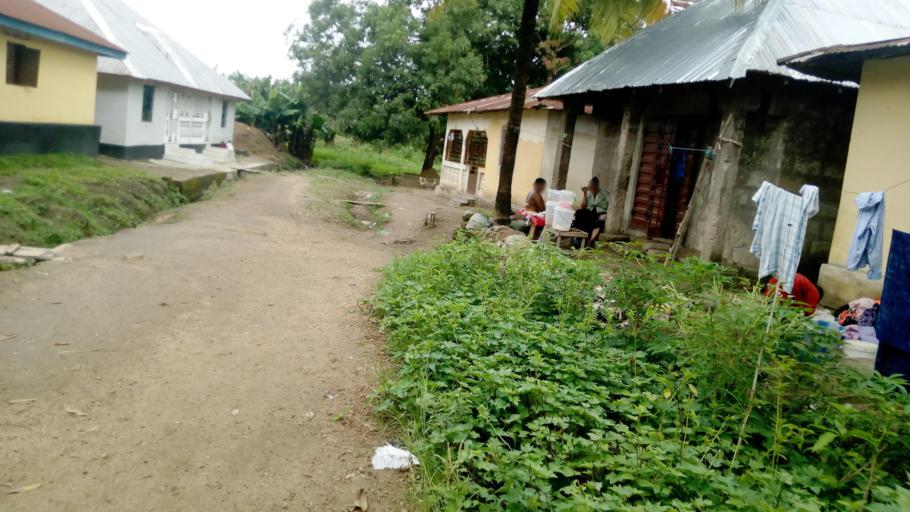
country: SL
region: Northern Province
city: Makeni
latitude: 8.8940
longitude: -12.0311
